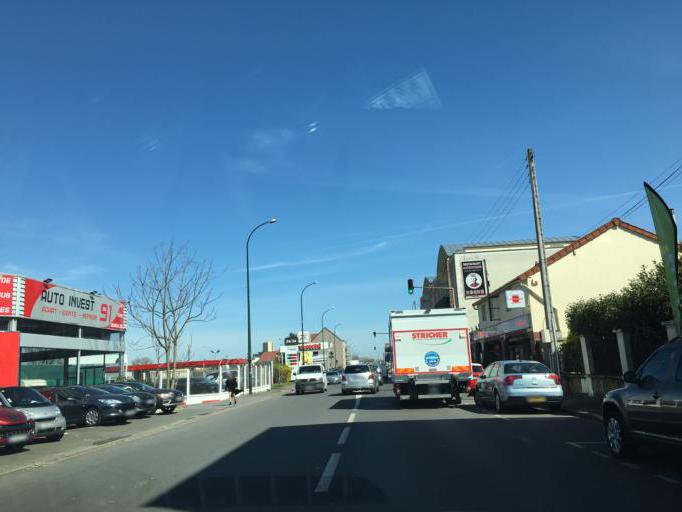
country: FR
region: Ile-de-France
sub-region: Departement de l'Essonne
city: Vigneux-sur-Seine
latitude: 48.6960
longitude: 2.4149
